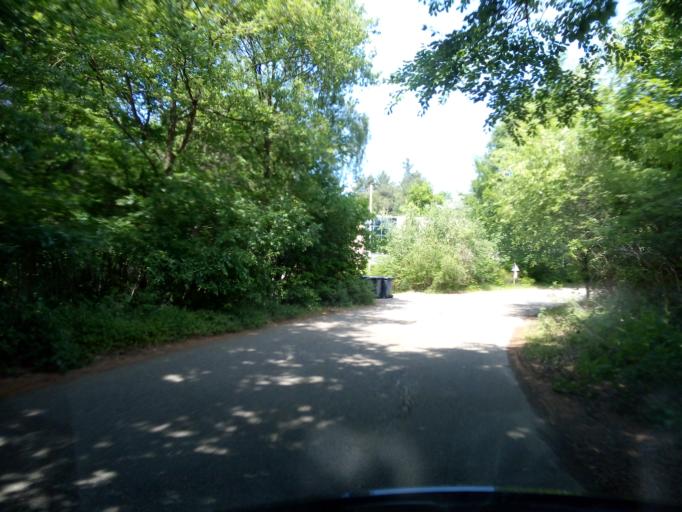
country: NL
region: North Holland
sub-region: Gemeente Laren
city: Laren
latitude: 52.2665
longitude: 5.2008
